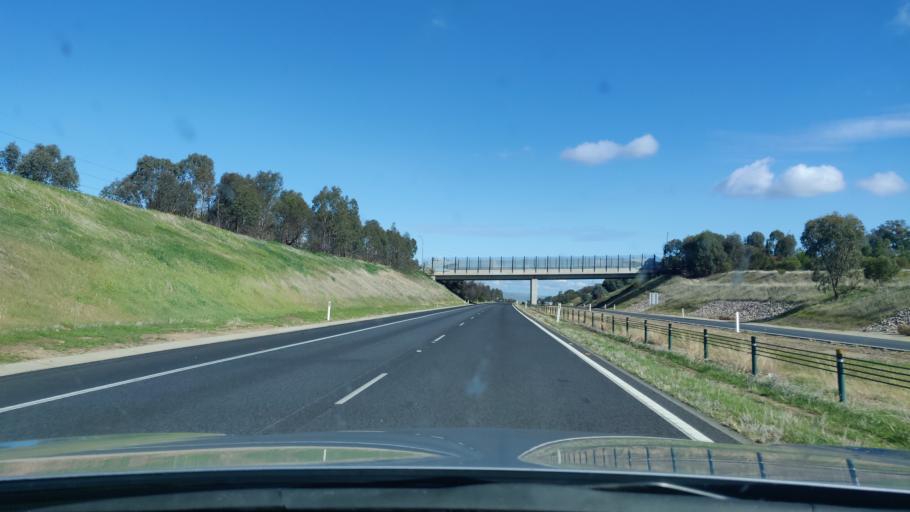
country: AU
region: New South Wales
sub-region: Albury Municipality
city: Lavington
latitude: -36.0514
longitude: 146.9606
